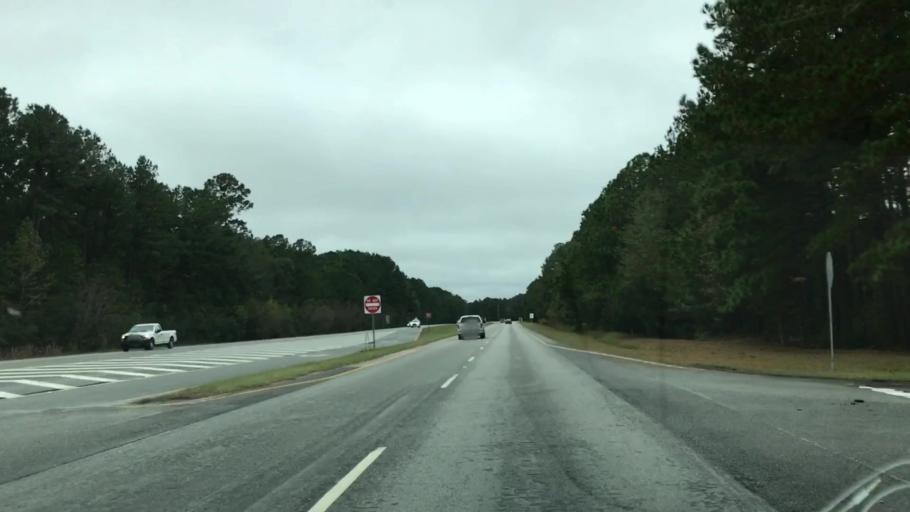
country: US
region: South Carolina
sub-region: Beaufort County
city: Bluffton
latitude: 32.3532
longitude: -80.9154
